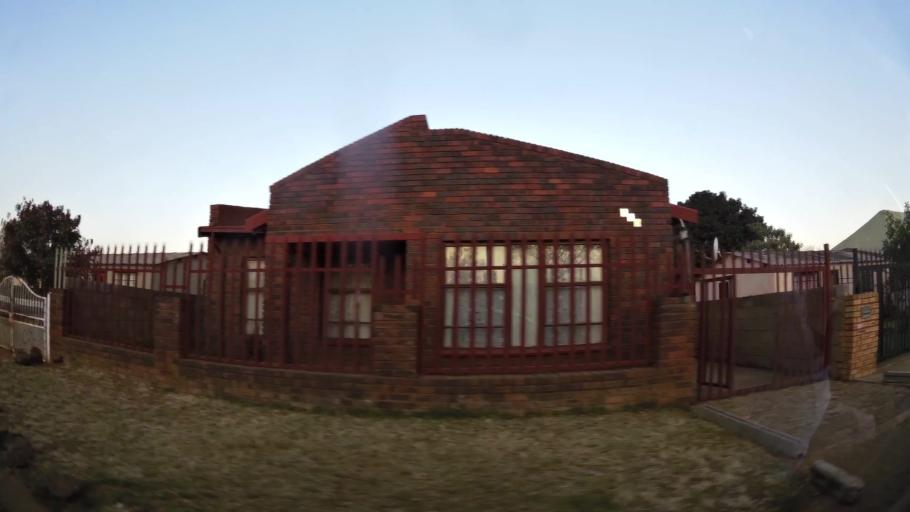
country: ZA
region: Gauteng
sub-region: West Rand District Municipality
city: Randfontein
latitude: -26.2026
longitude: 27.7135
